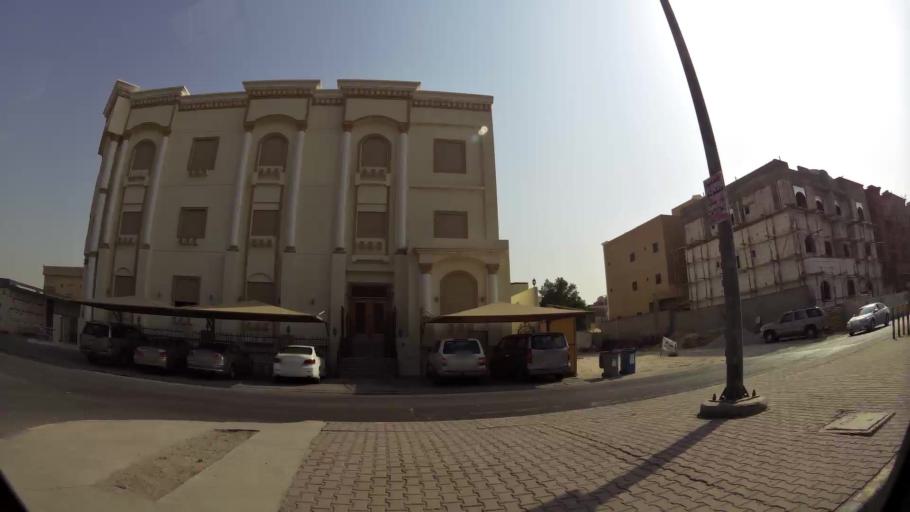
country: KW
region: Al Asimah
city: Ar Rabiyah
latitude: 29.2752
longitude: 47.8941
